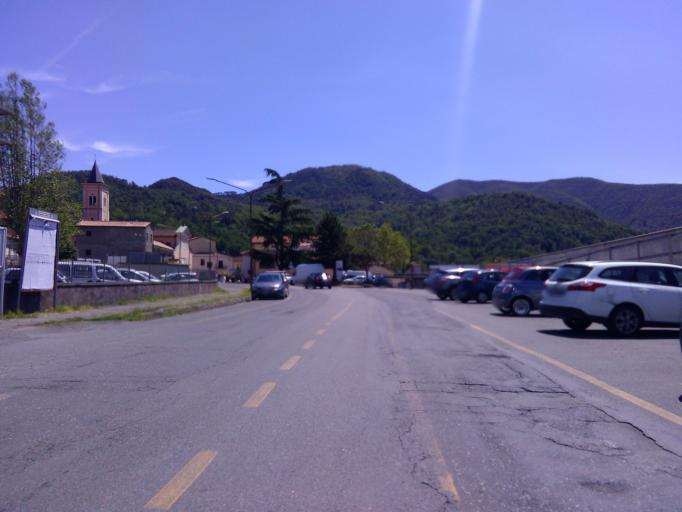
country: IT
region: Tuscany
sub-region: Provincia di Massa-Carrara
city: Aulla
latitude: 44.2086
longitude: 9.9672
